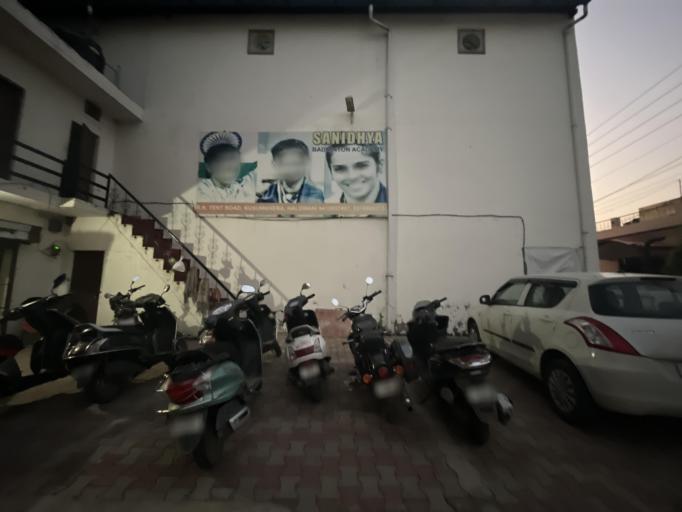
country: IN
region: Uttarakhand
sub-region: Naini Tal
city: Haldwani
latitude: 29.2133
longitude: 79.5014
